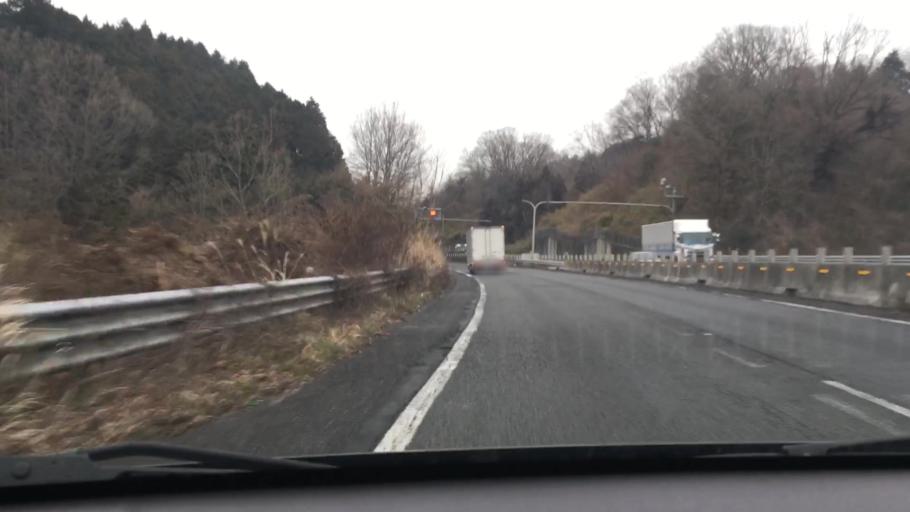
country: JP
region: Mie
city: Nabari
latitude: 34.6843
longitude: 136.0460
